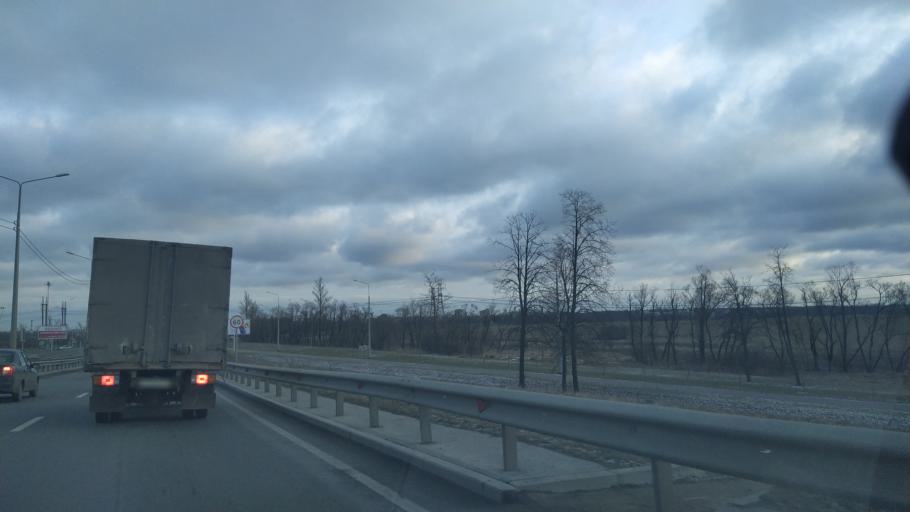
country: RU
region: St.-Petersburg
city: Pushkin
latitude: 59.7544
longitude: 30.3872
